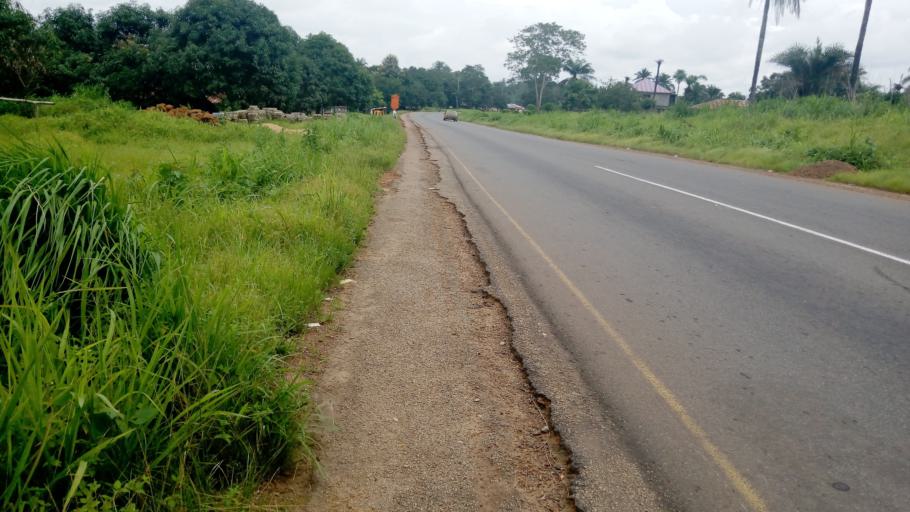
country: SL
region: Northern Province
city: Port Loko
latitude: 8.5039
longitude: -12.7593
